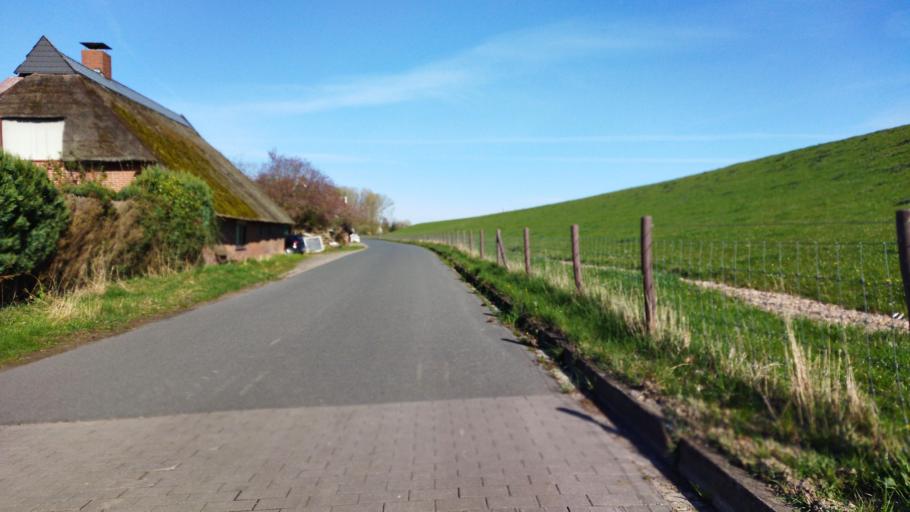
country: DE
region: Lower Saxony
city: Neuenkirchen
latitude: 53.2050
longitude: 8.4905
